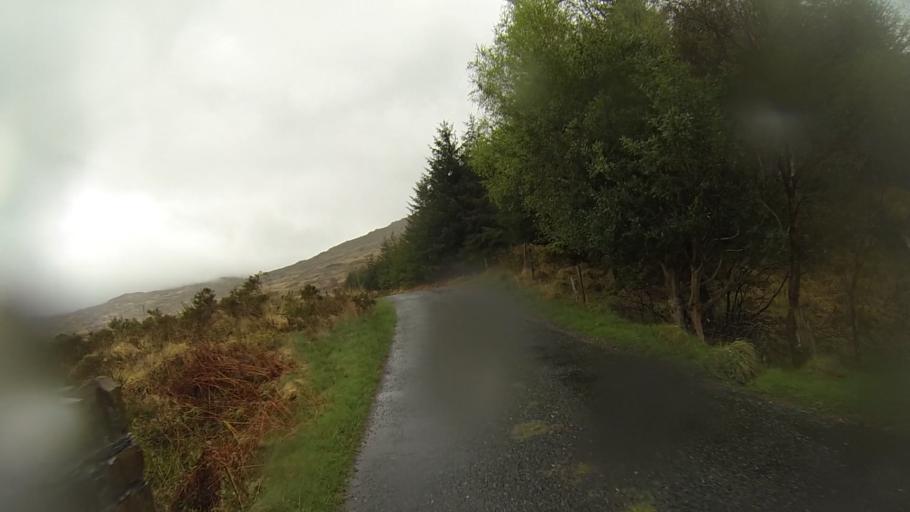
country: IE
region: Munster
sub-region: Ciarrai
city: Kenmare
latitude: 51.9476
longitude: -9.6874
